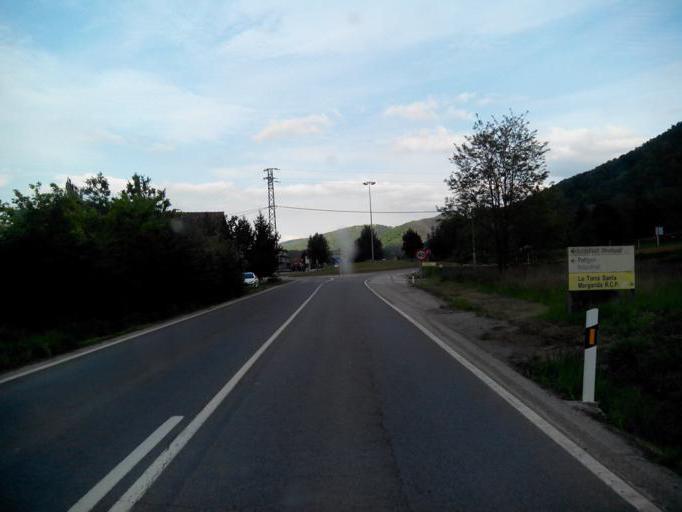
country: ES
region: Catalonia
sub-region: Provincia de Girona
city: MeteOlot
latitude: 42.2099
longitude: 2.4694
